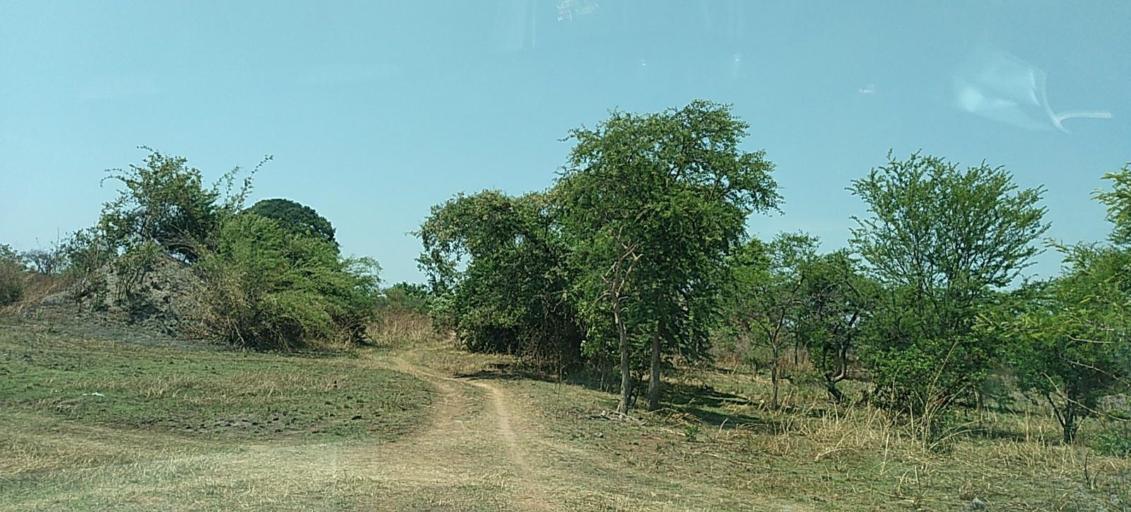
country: ZM
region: Copperbelt
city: Luanshya
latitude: -12.9914
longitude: 28.3253
